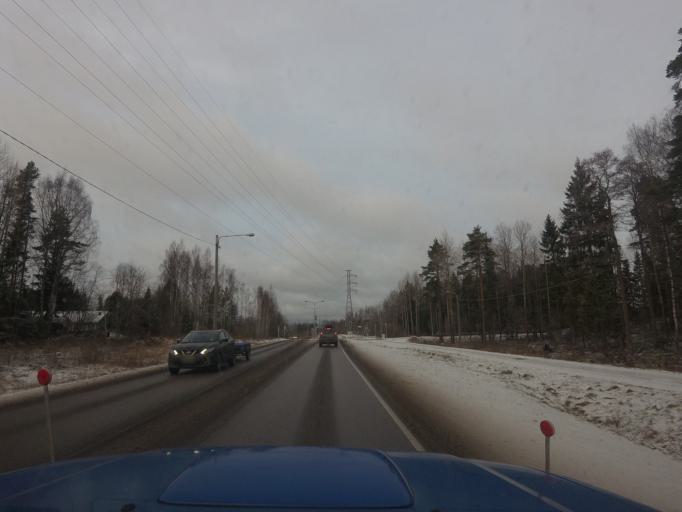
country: FI
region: Uusimaa
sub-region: Helsinki
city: Espoo
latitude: 60.1794
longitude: 24.6100
